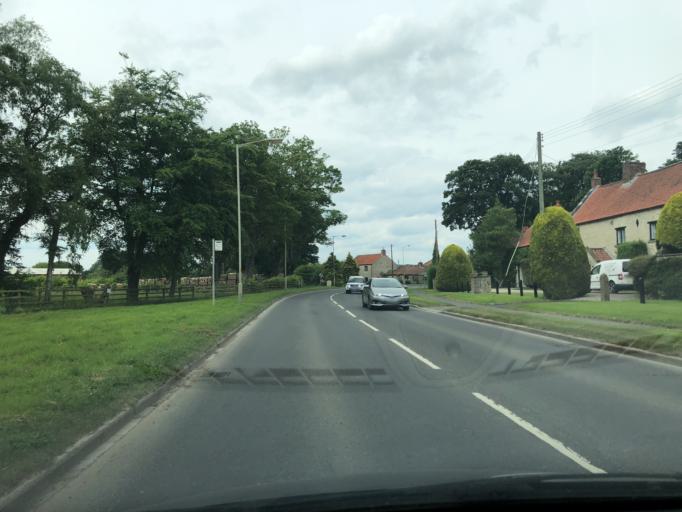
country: GB
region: England
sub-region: North Yorkshire
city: Pickering
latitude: 54.2504
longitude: -0.7931
